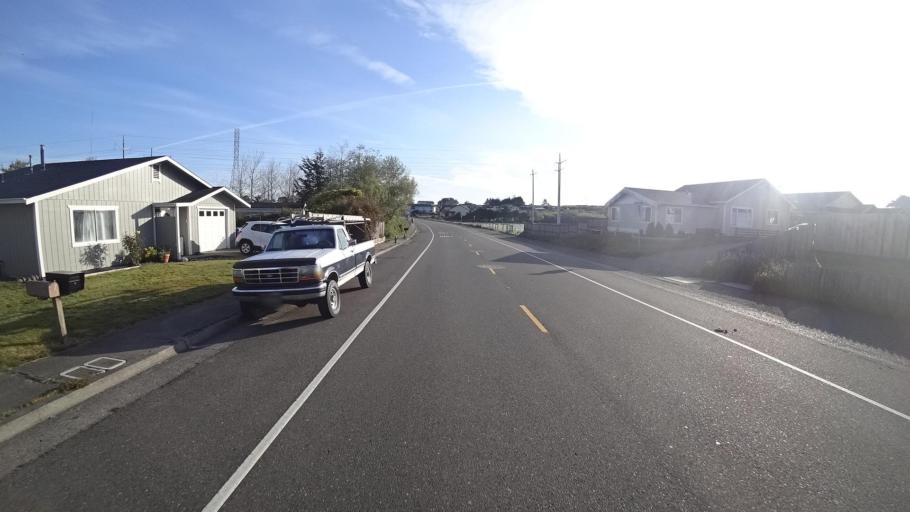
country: US
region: California
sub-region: Humboldt County
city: Humboldt Hill
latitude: 40.7372
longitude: -124.2013
